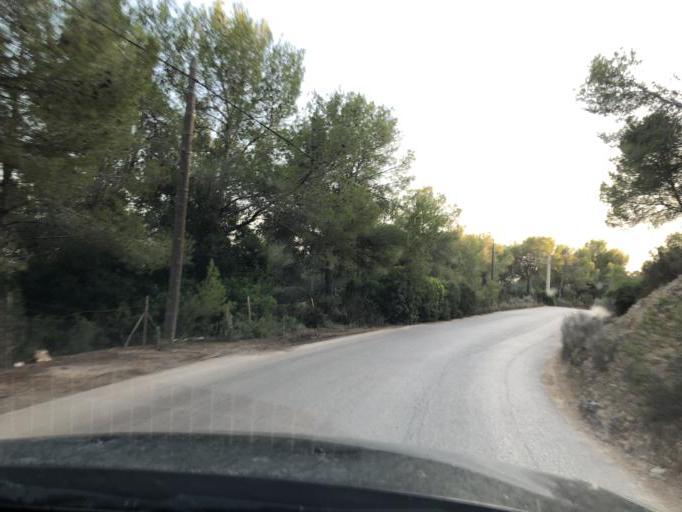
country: ES
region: Balearic Islands
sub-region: Illes Balears
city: Santa Ponsa
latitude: 39.5359
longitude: 2.4812
